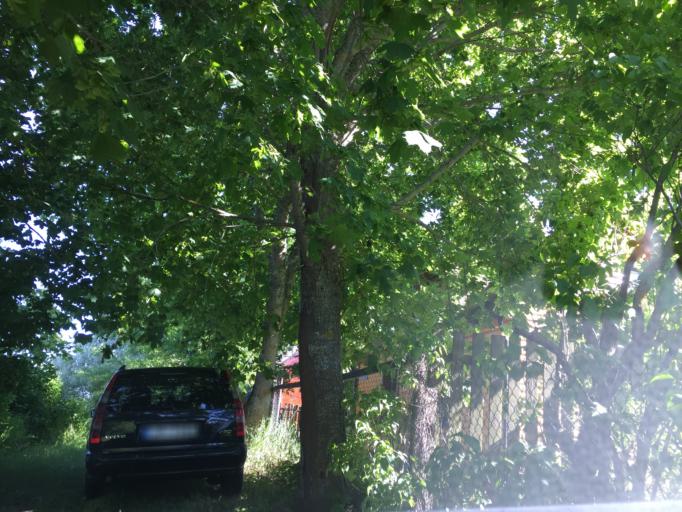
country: LV
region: Rojas
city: Roja
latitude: 57.4580
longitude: 22.8869
